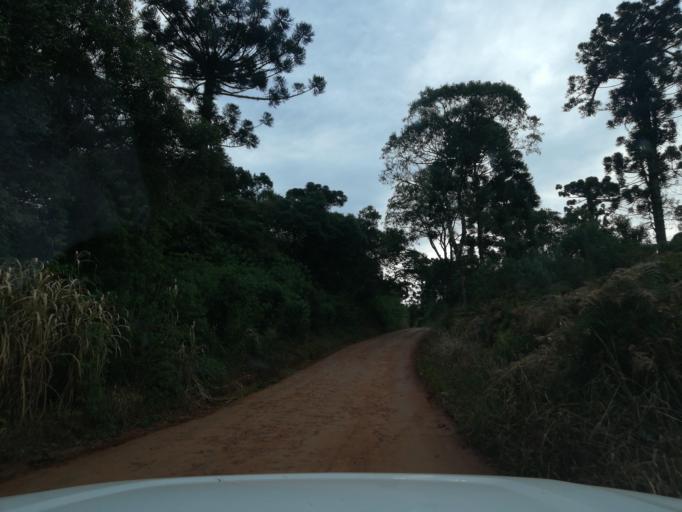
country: AR
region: Misiones
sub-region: Departamento de San Pedro
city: San Pedro
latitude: -26.6339
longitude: -54.0992
